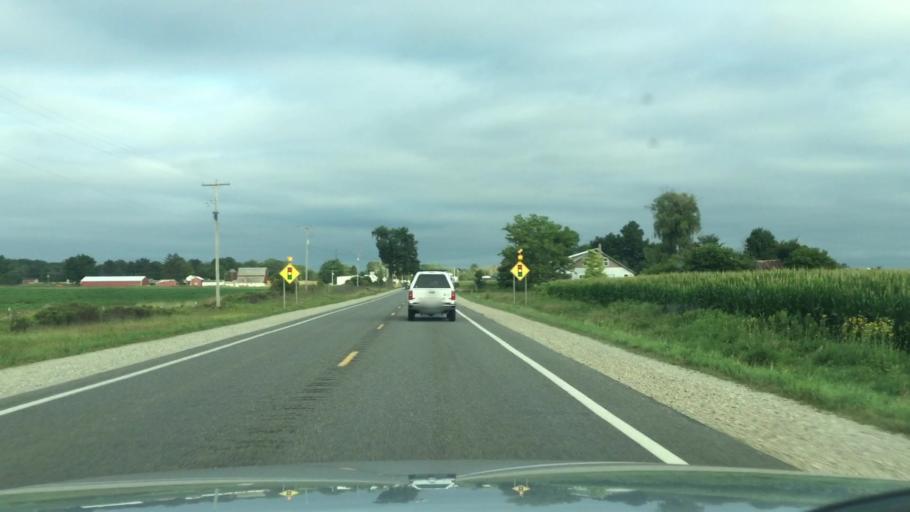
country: US
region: Michigan
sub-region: Montcalm County
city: Stanton
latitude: 43.1783
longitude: -85.0665
